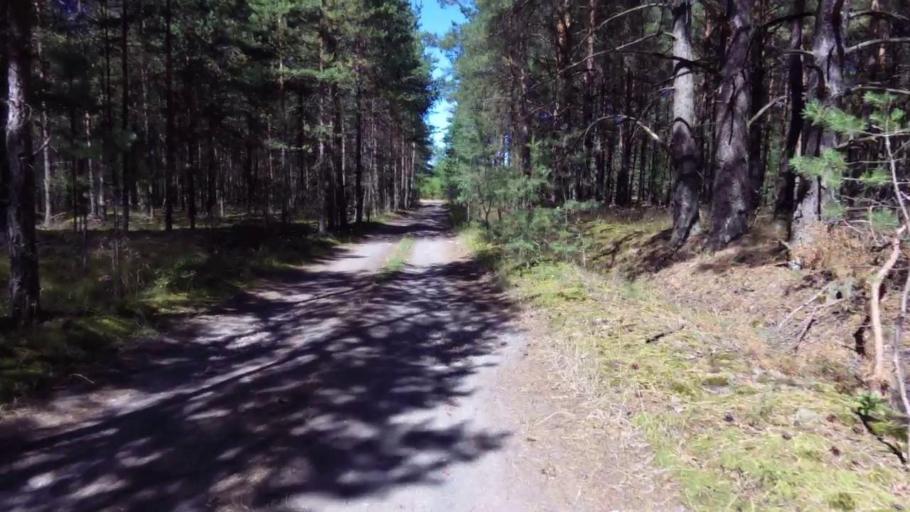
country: PL
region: West Pomeranian Voivodeship
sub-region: Powiat szczecinecki
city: Borne Sulinowo
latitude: 53.5870
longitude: 16.4957
